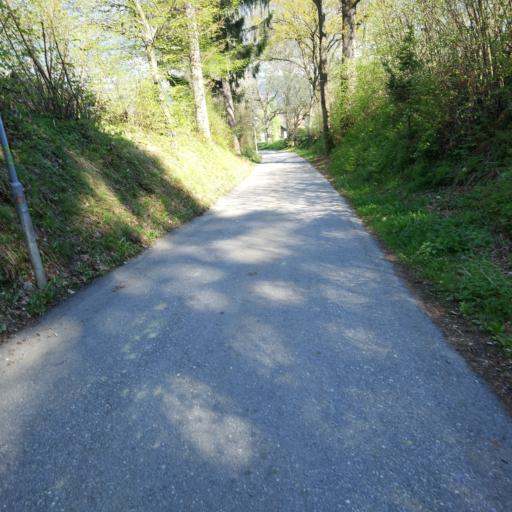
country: AT
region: Carinthia
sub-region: Politischer Bezirk Feldkirchen
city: Steindorf am Ossiacher See
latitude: 46.6820
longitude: 14.0032
